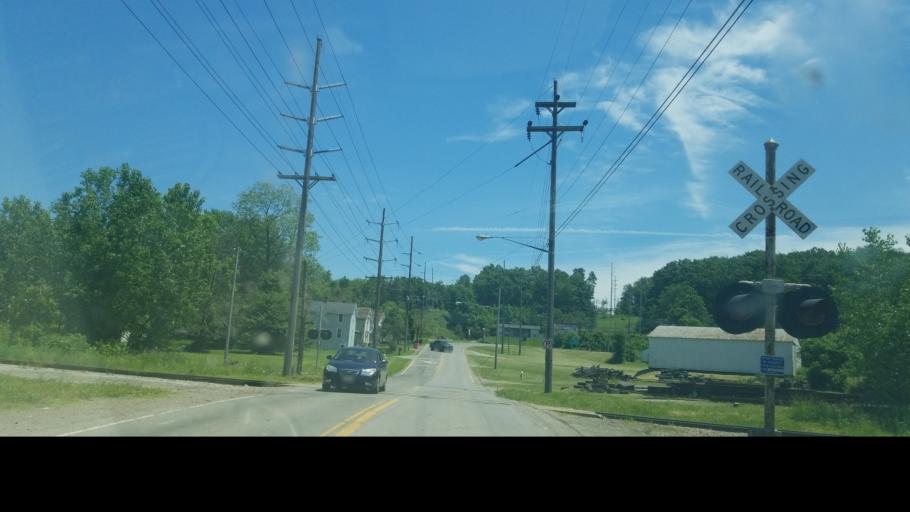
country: US
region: Ohio
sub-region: Richland County
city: Mansfield
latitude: 40.7772
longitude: -82.5076
